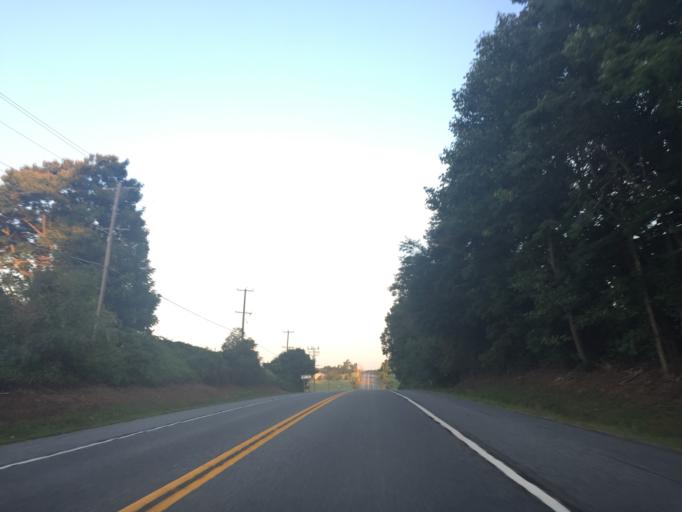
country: US
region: Pennsylvania
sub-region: York County
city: Susquehanna Trails
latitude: 39.6961
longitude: -76.3182
